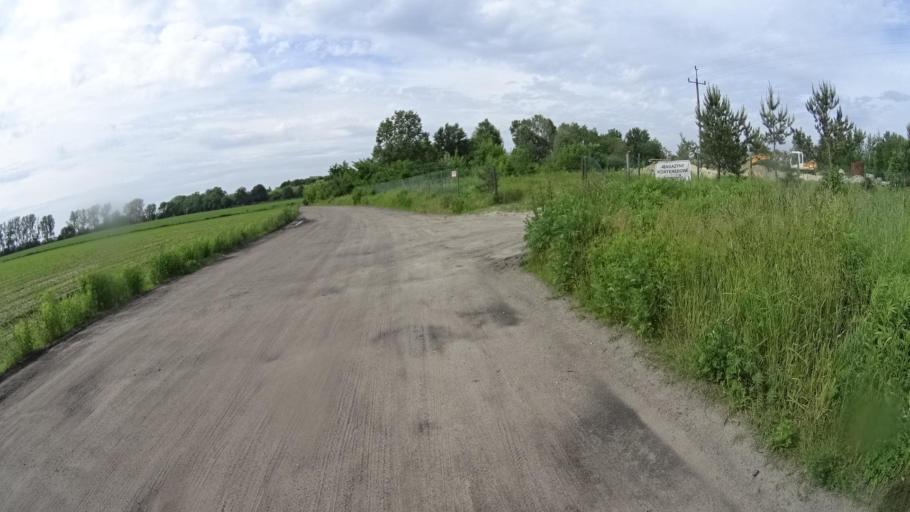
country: PL
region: Masovian Voivodeship
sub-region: Powiat warszawski zachodni
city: Jozefow
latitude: 52.1942
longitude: 20.7423
